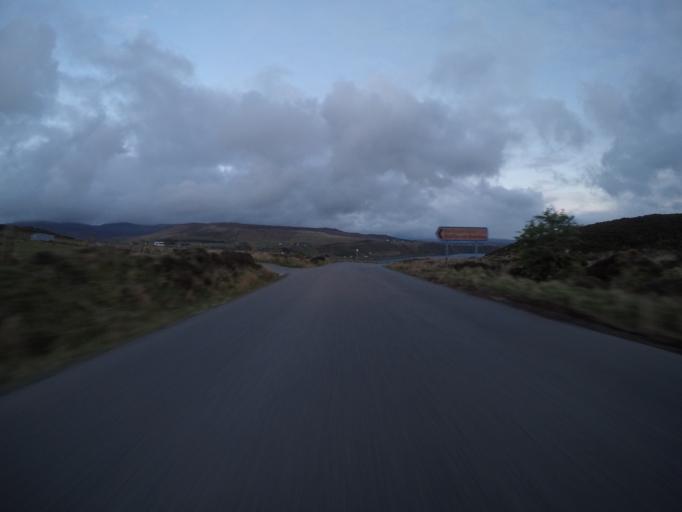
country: GB
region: Scotland
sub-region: Highland
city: Portree
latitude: 57.5944
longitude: -6.3734
